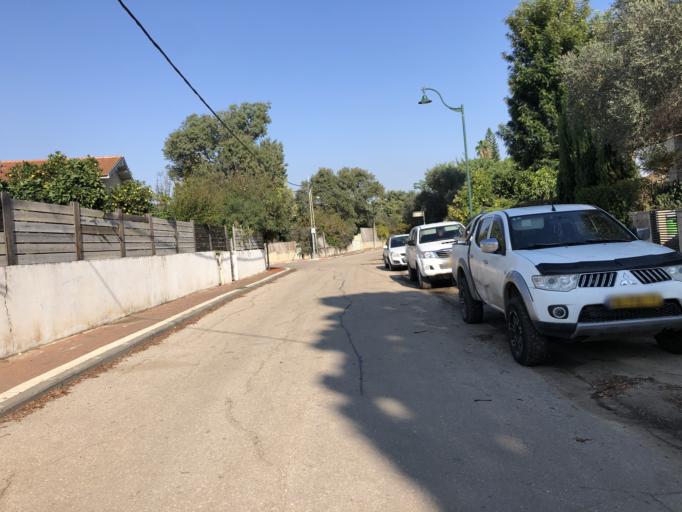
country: IL
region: Central District
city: Jaljulya
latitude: 32.1324
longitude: 34.9258
